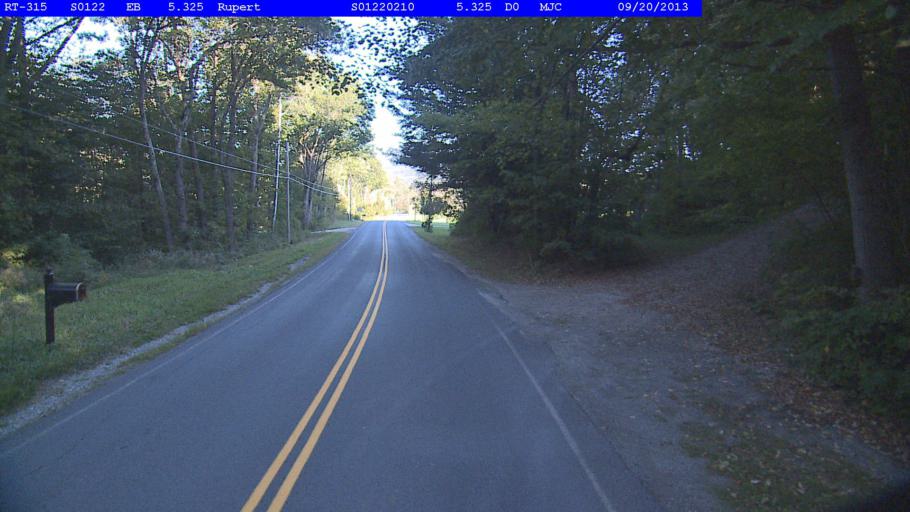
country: US
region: Vermont
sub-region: Bennington County
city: Manchester Center
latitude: 43.2752
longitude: -73.1341
